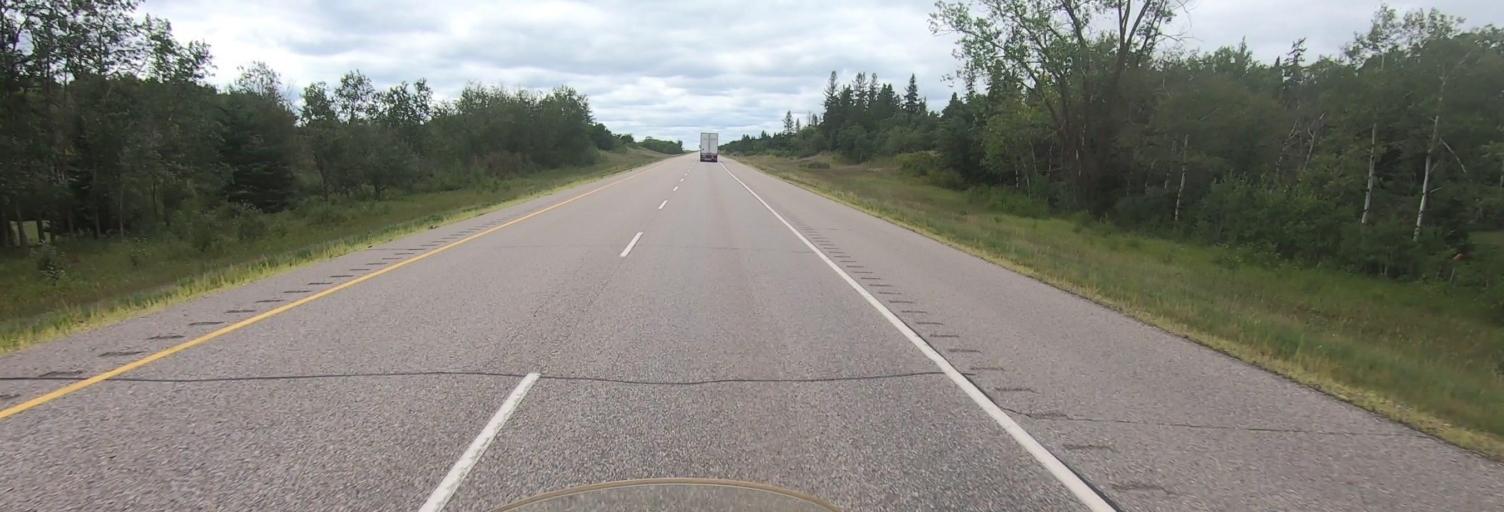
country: CA
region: Manitoba
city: Carberry
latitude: 49.9016
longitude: -99.2560
